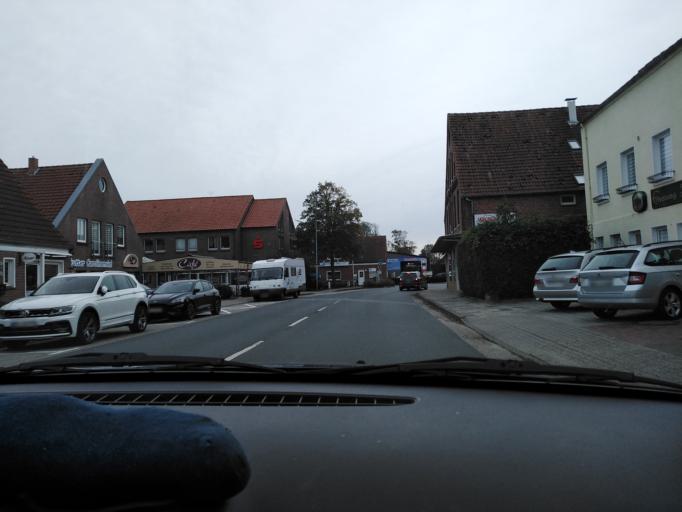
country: DE
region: Lower Saxony
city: Werdum
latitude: 53.6910
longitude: 7.8030
